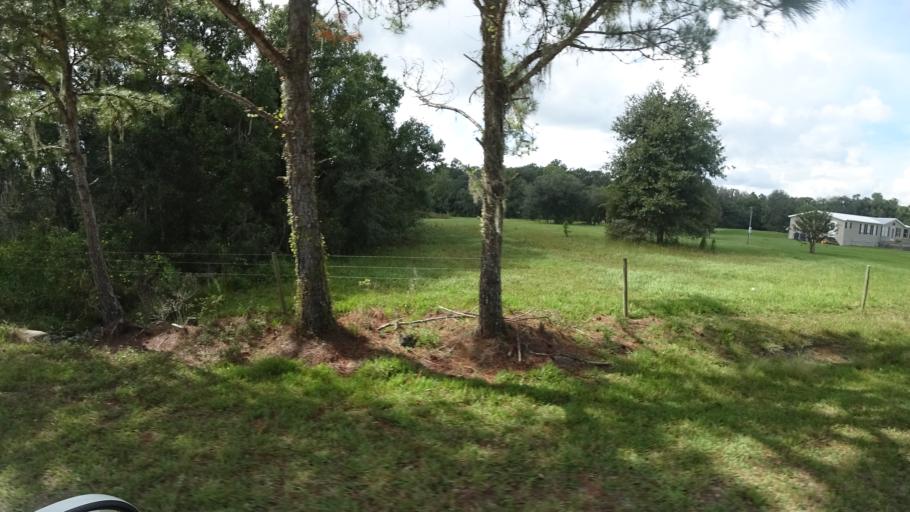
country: US
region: Florida
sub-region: Hillsborough County
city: Wimauma
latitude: 27.5468
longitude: -82.1745
